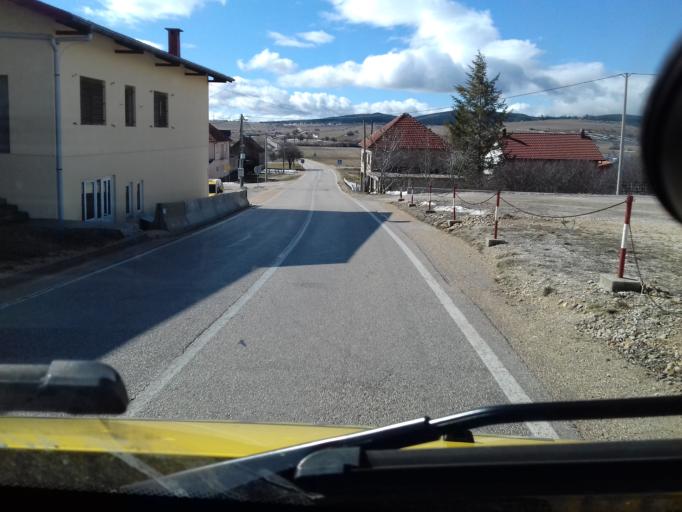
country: BA
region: Federation of Bosnia and Herzegovina
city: Tomislavgrad
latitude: 43.7629
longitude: 17.2361
